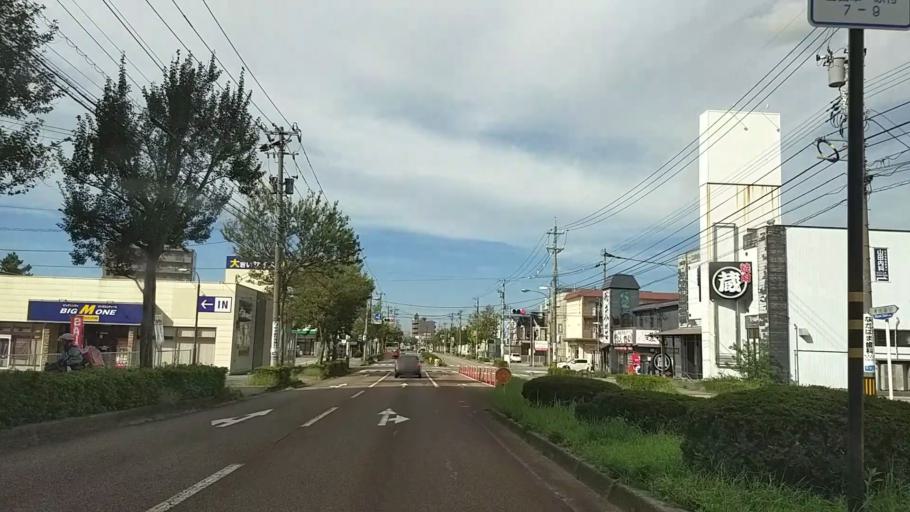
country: JP
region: Ishikawa
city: Nonoichi
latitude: 36.5324
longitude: 136.6386
